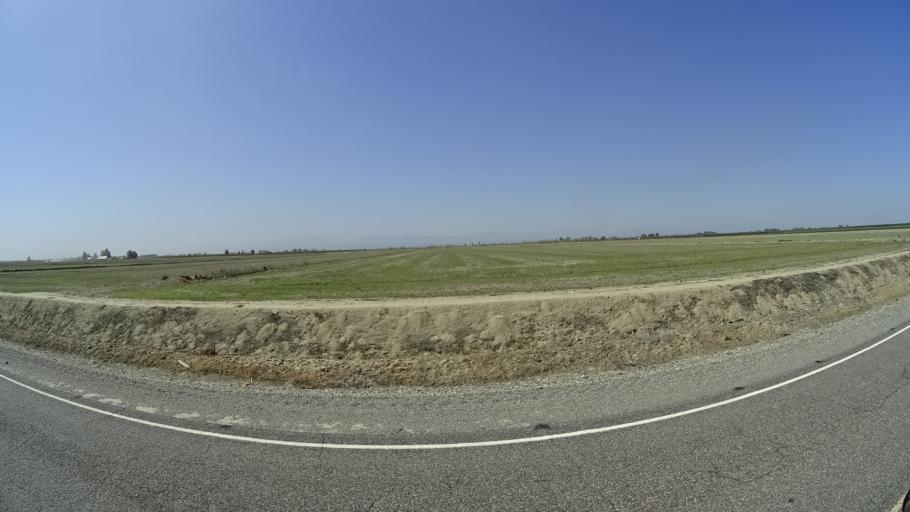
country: US
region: California
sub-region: Glenn County
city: Willows
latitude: 39.5628
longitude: -122.1369
